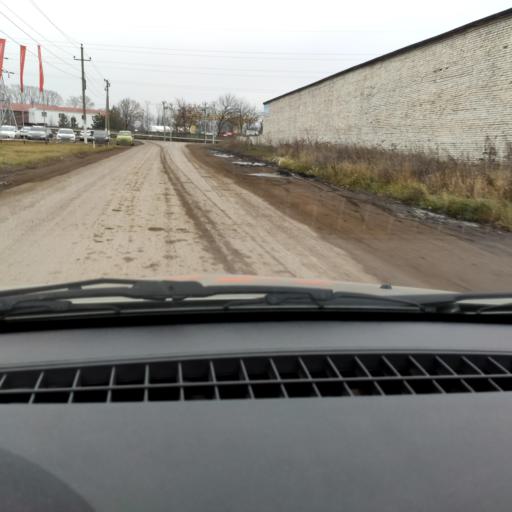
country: RU
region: Bashkortostan
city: Ufa
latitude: 54.5801
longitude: 55.9003
